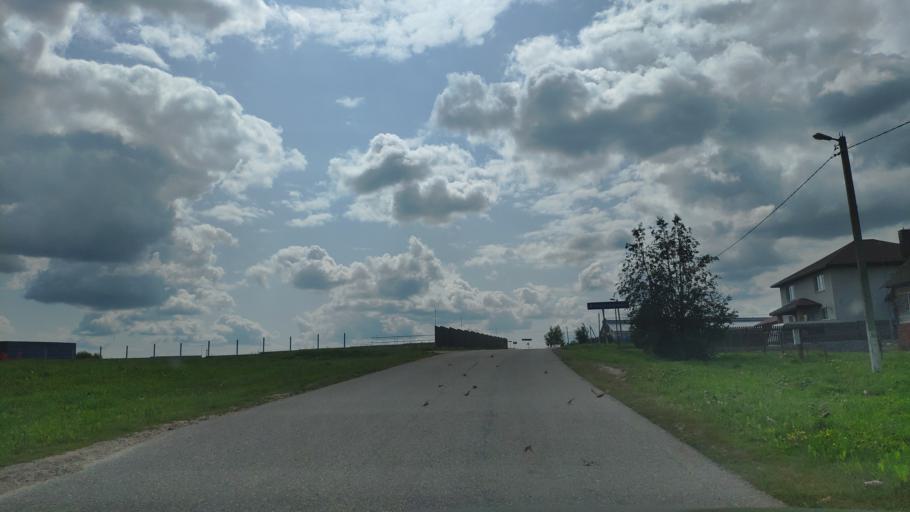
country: BY
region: Minsk
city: Khatsyezhyna
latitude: 53.8641
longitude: 27.3157
